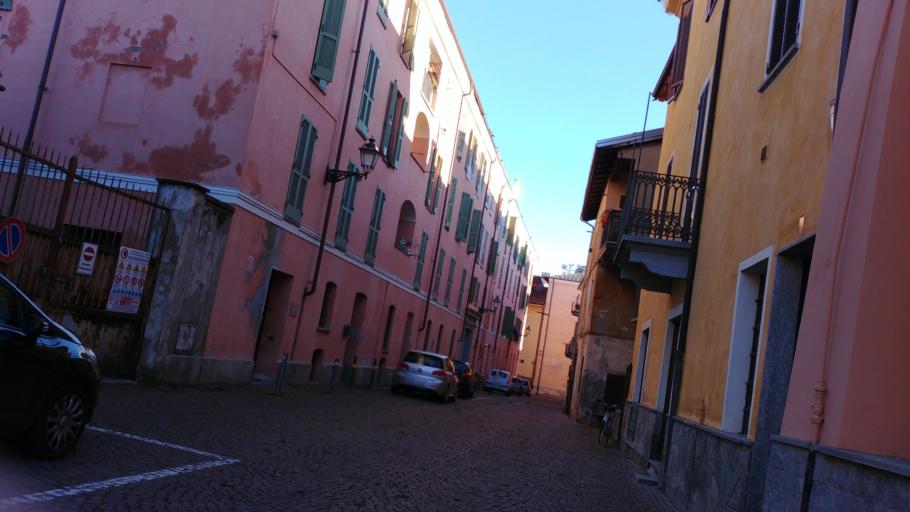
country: IT
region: Piedmont
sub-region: Provincia di Cuneo
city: Cuneo
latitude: 44.3949
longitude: 7.5515
